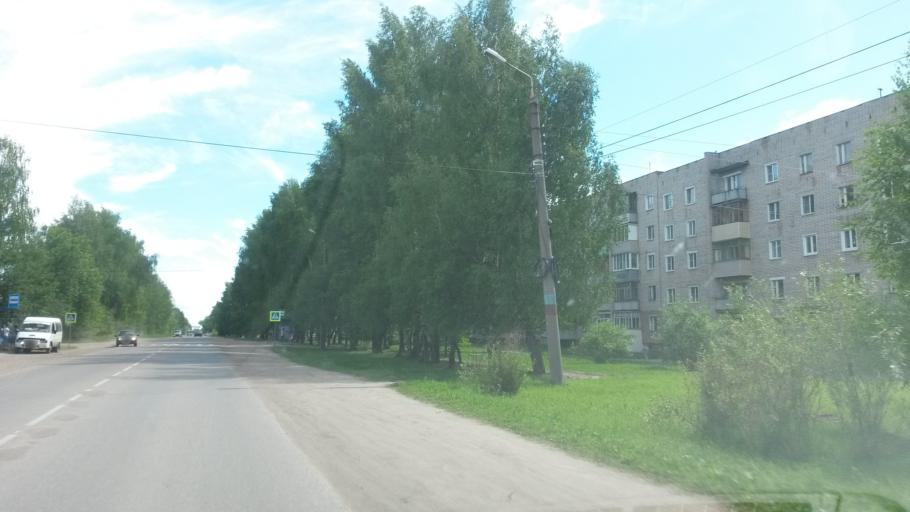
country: RU
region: Ivanovo
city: Zavolzhsk
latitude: 57.4789
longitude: 42.1506
